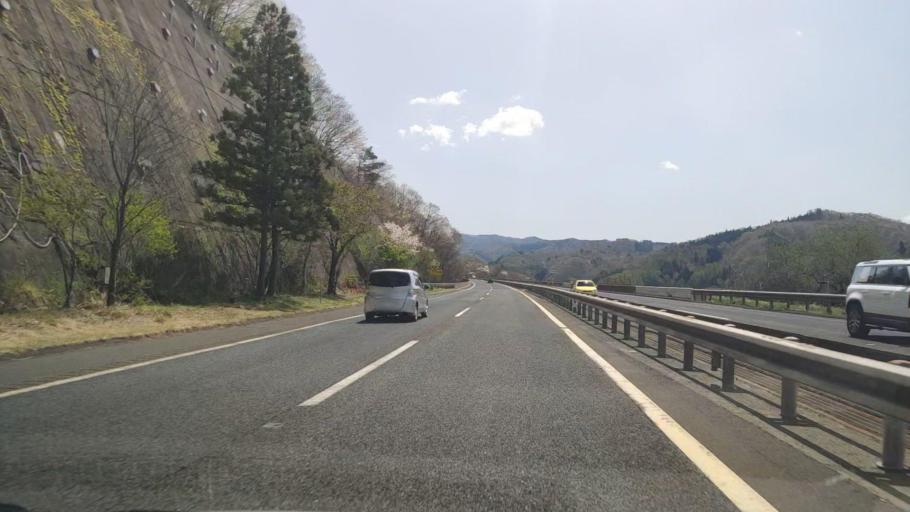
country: JP
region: Iwate
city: Ichinohe
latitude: 40.2246
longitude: 141.3287
